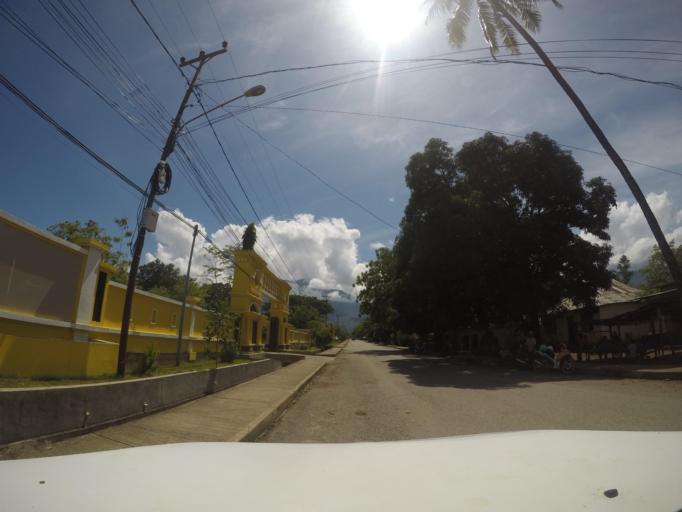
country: TL
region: Bobonaro
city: Maliana
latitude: -8.9896
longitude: 125.2082
